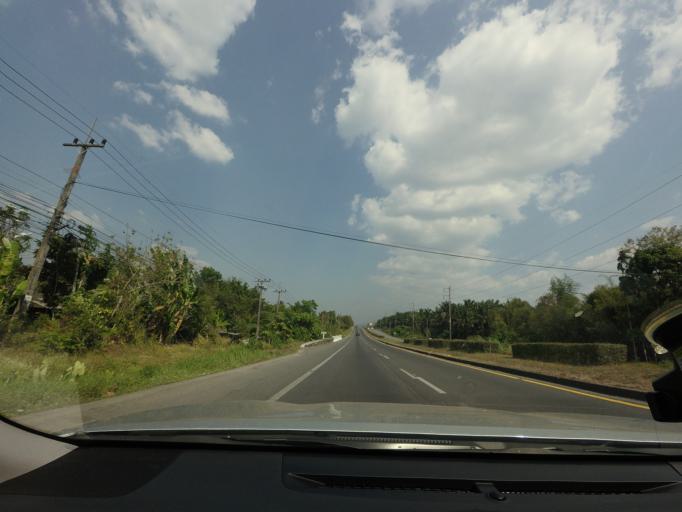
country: TH
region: Phangnga
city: Thap Put
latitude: 8.5094
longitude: 98.6489
